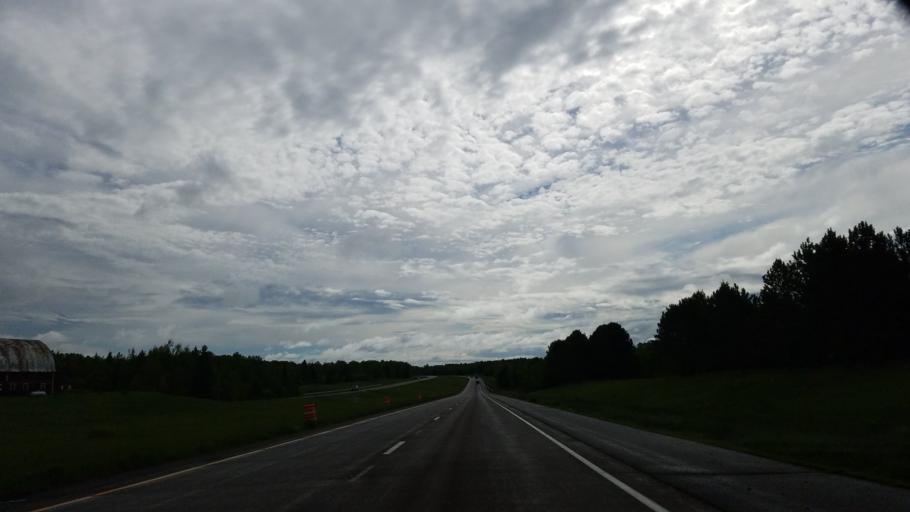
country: US
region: Minnesota
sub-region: Lake County
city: Two Harbors
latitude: 46.9289
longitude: -91.8424
